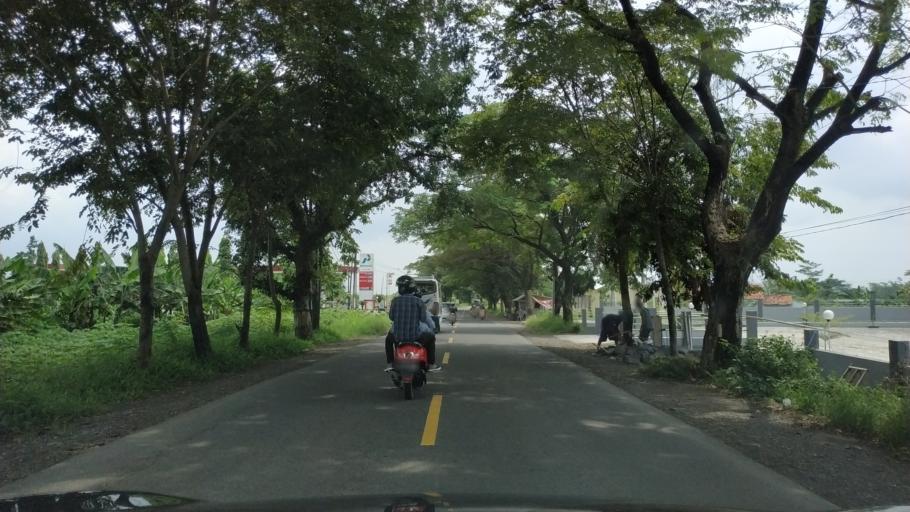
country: ID
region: Central Java
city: Lebaksiu
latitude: -7.0314
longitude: 109.1441
